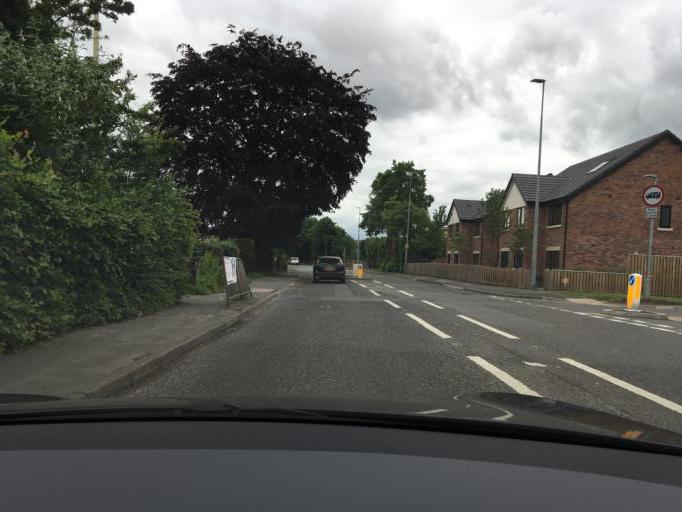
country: GB
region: England
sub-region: Cheshire East
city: Poynton
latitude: 53.3445
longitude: -2.1255
